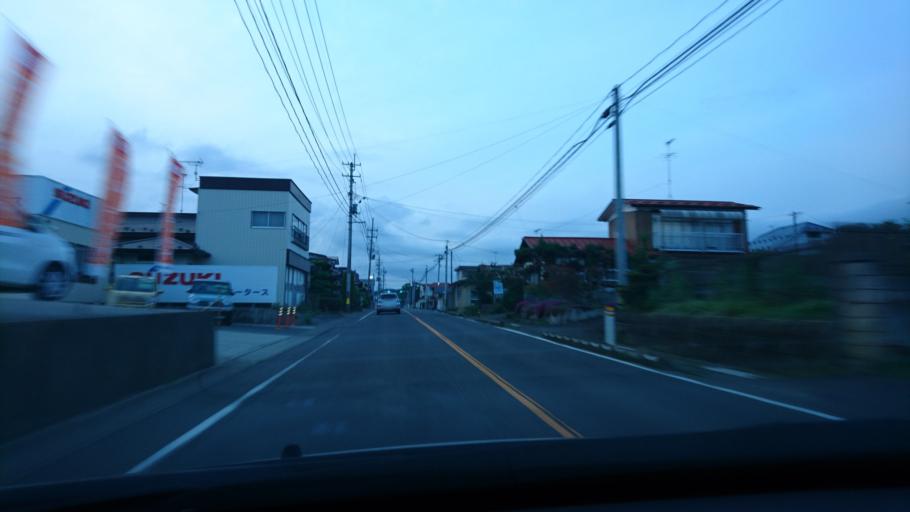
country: JP
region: Iwate
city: Ichinoseki
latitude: 38.8183
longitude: 140.9857
